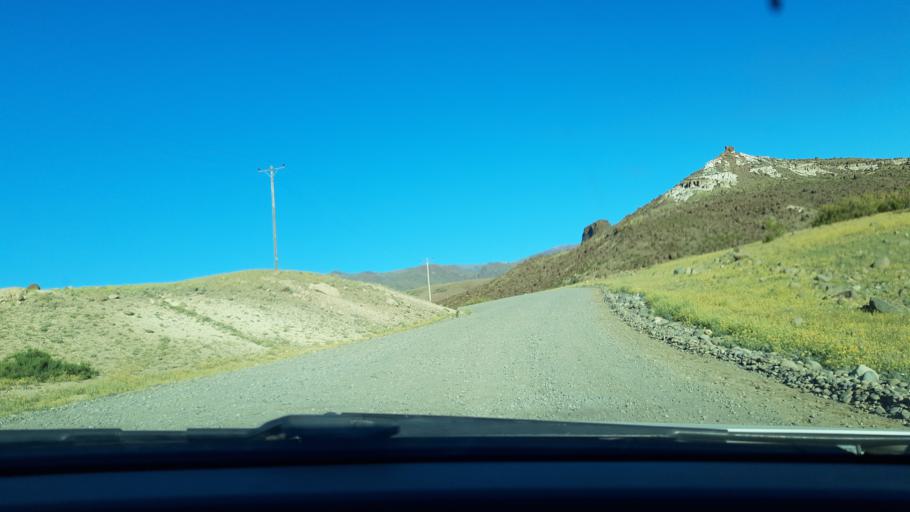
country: AR
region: Neuquen
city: Las Ovejas
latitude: -36.8222
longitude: -70.7063
